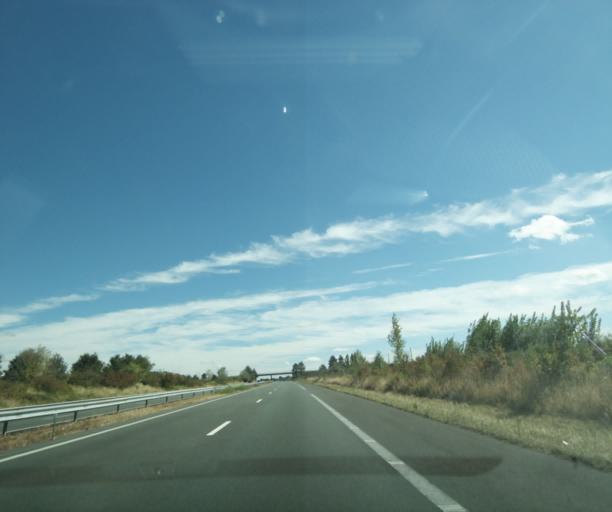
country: FR
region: Aquitaine
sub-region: Departement du Lot-et-Garonne
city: Sainte-Colombe-en-Bruilhois
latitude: 44.1918
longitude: 0.5197
